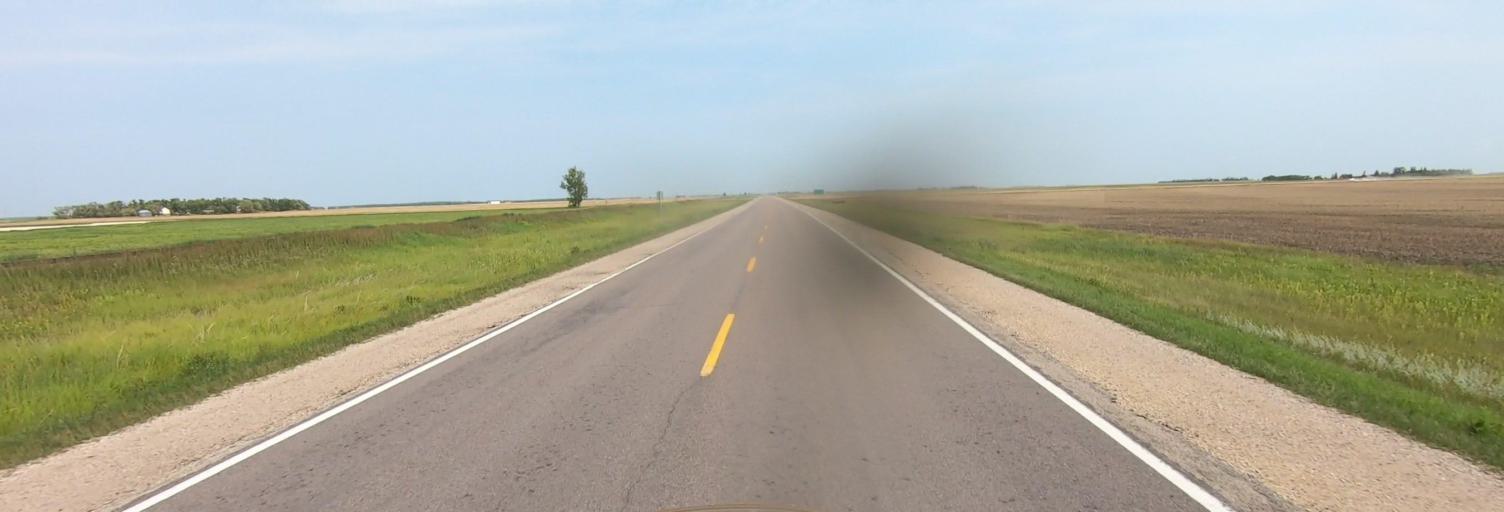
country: CA
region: Manitoba
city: Morris
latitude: 49.6179
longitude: -97.3184
